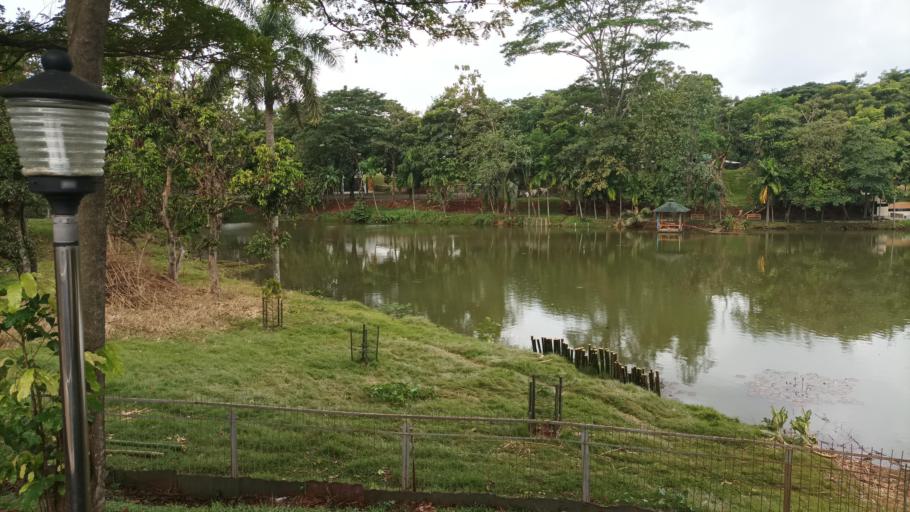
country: ID
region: West Java
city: Depok
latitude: -6.4332
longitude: 106.8418
